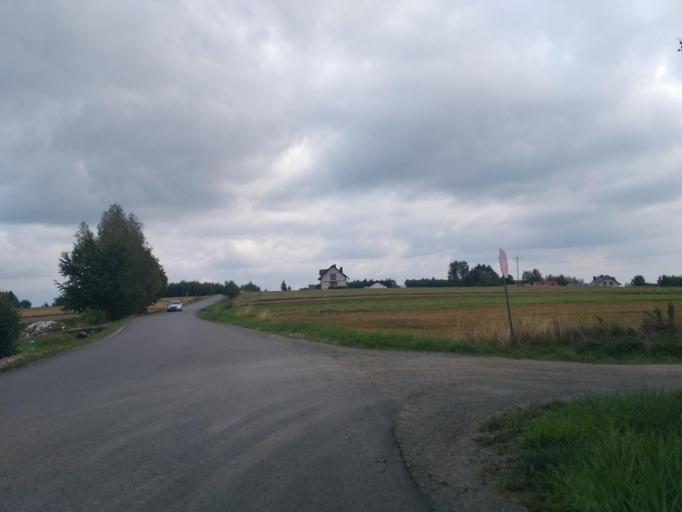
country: PL
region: Subcarpathian Voivodeship
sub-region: Powiat rzeszowski
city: Chmielnik
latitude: 50.0052
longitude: 22.1430
